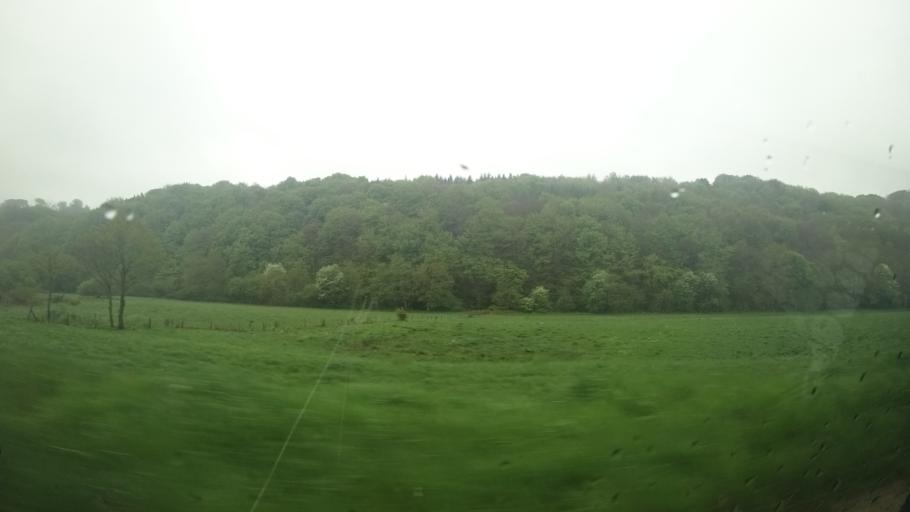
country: FR
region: Midi-Pyrenees
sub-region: Departement de l'Aveyron
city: Salles-Curan
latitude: 44.2657
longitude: 2.8863
